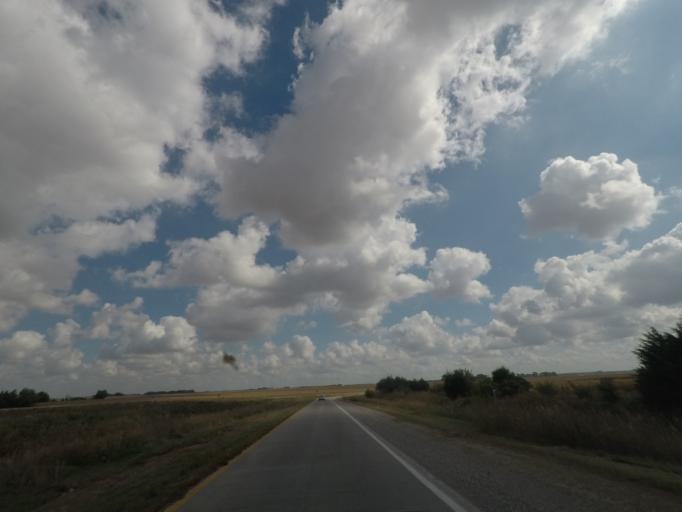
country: US
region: Iowa
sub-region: Story County
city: Nevada
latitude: 42.0068
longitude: -93.4326
